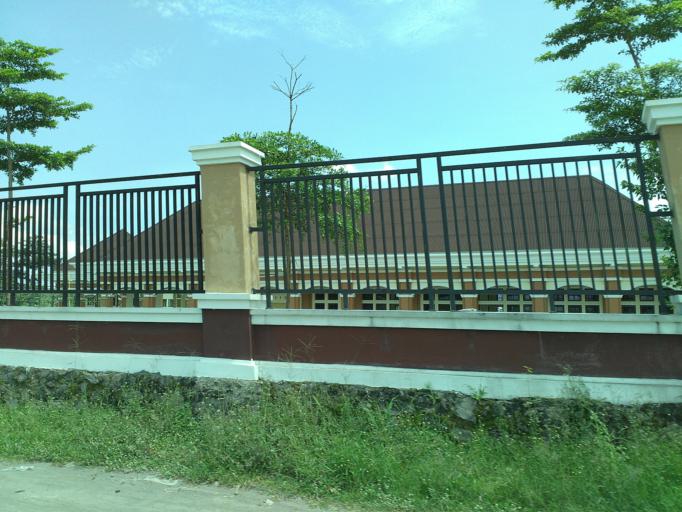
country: ID
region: Central Java
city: Klaten
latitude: -7.7032
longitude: 110.5953
